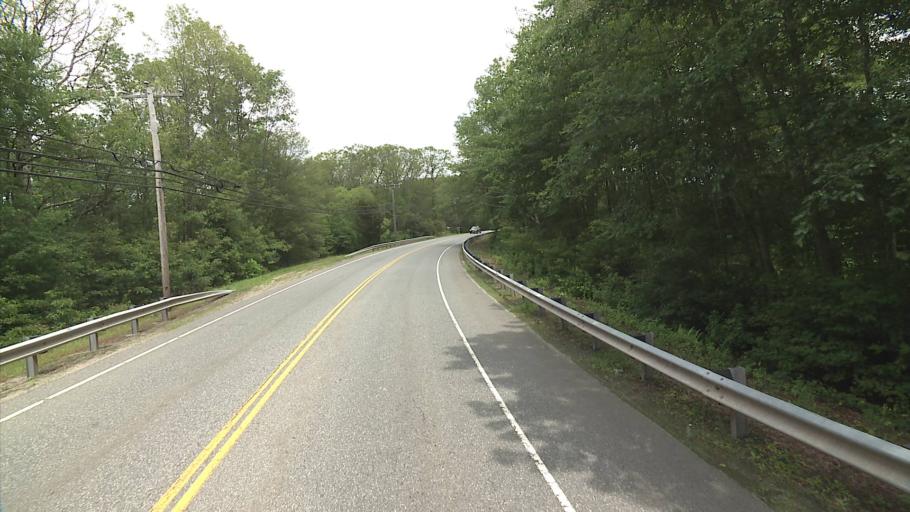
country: US
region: Connecticut
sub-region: Middlesex County
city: Deep River Center
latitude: 41.3793
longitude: -72.4551
